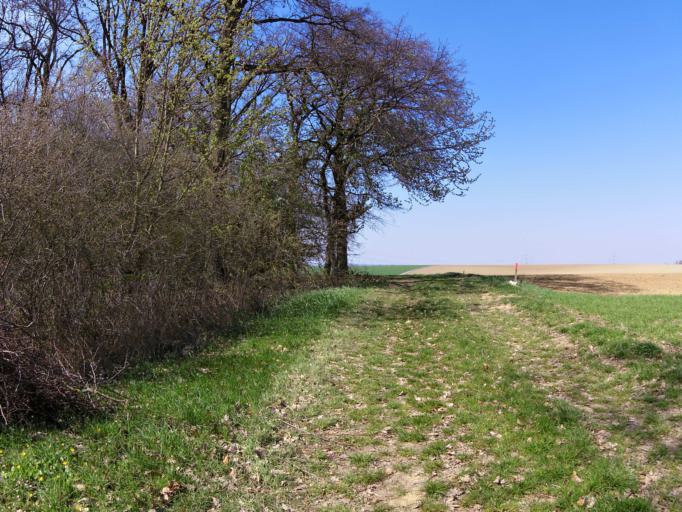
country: DE
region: Bavaria
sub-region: Regierungsbezirk Unterfranken
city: Biebelried
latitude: 49.7824
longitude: 10.0587
